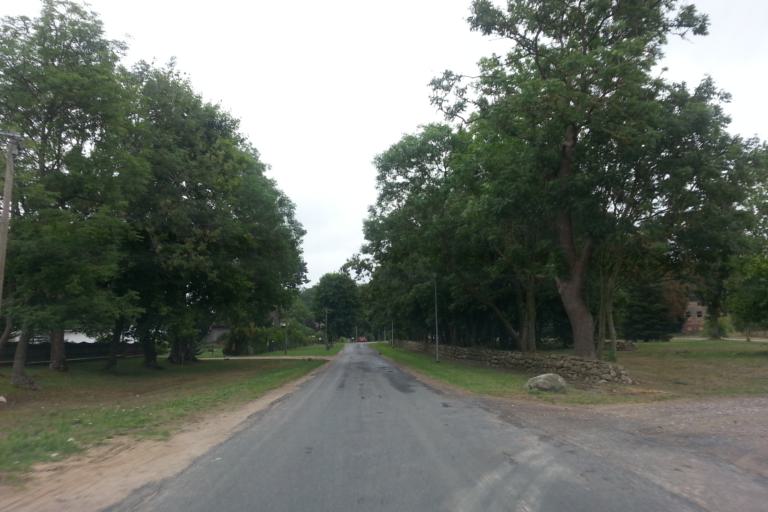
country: DE
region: Mecklenburg-Vorpommern
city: Ferdinandshof
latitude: 53.6566
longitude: 13.9308
